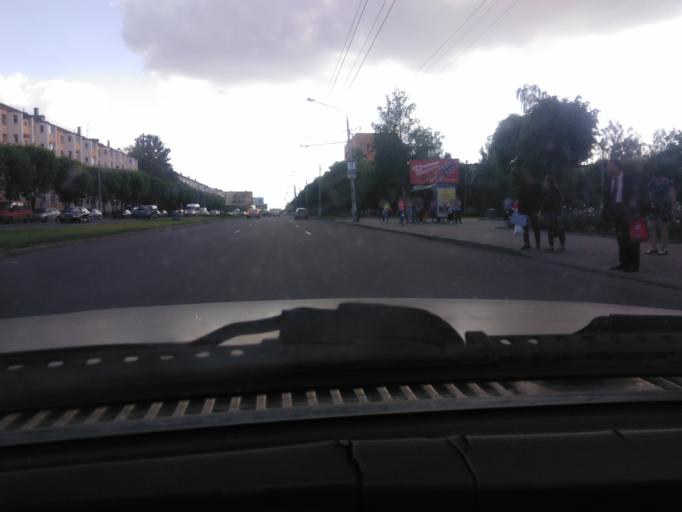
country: BY
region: Mogilev
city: Mahilyow
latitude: 53.9117
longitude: 30.3164
